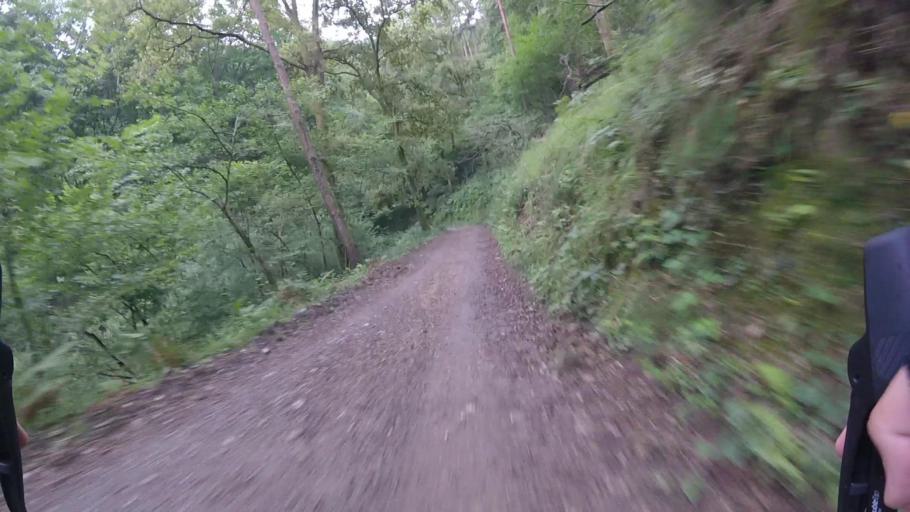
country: ES
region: Navarre
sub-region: Provincia de Navarra
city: Arano
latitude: 43.2541
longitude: -1.8550
